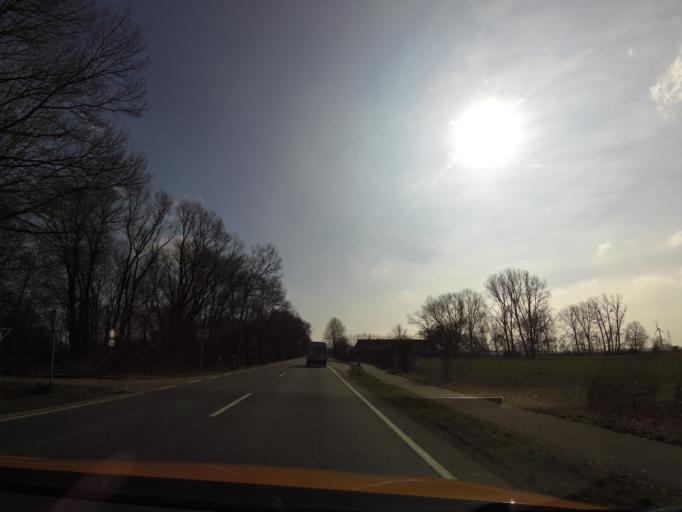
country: DE
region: Lower Saxony
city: Elsfleth
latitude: 53.2108
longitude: 8.4441
